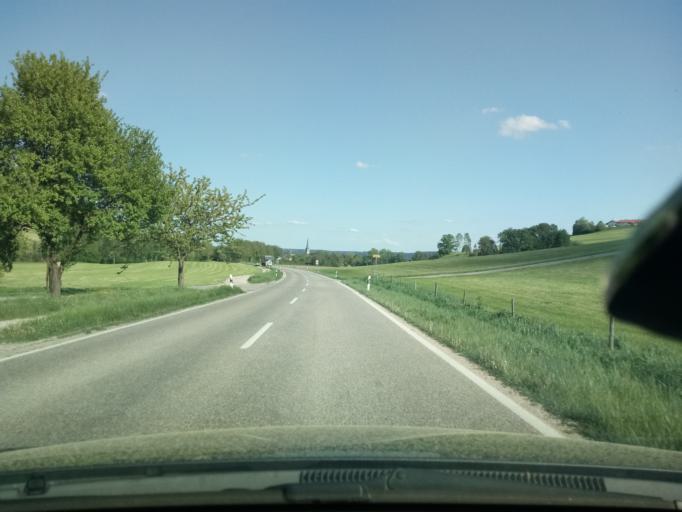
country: DE
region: Bavaria
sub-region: Upper Bavaria
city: Aschau am Inn
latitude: 48.2025
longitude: 12.3337
